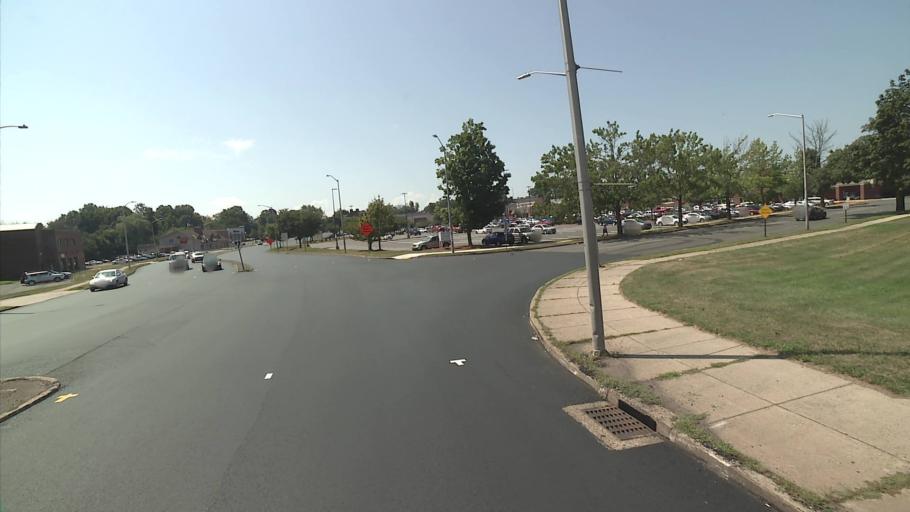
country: US
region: Connecticut
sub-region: New Haven County
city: East Haven
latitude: 41.2790
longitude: -72.8674
